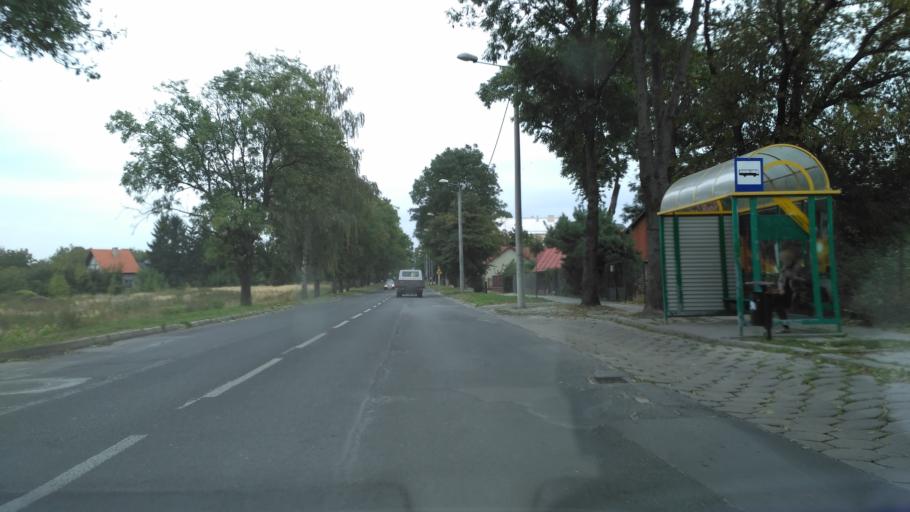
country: PL
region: Lublin Voivodeship
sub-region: Chelm
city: Chelm
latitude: 51.1438
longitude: 23.4440
